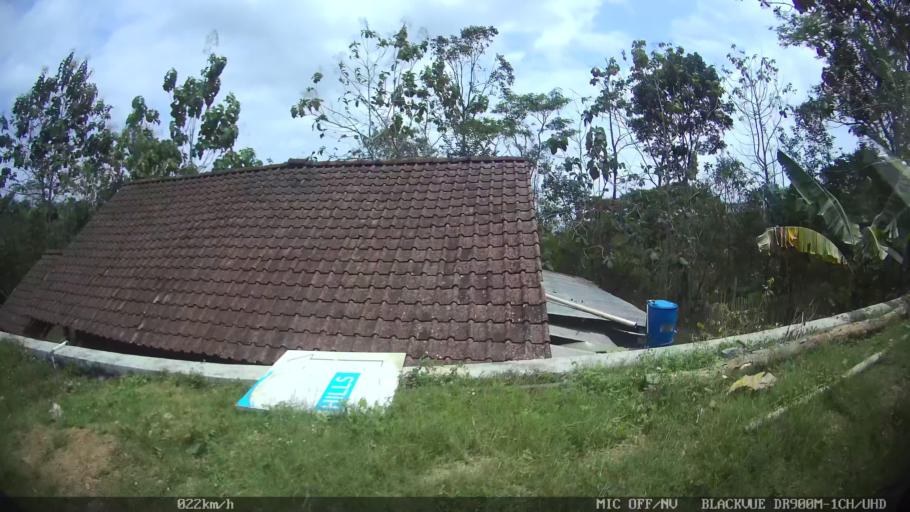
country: ID
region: Central Java
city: Candi Prambanan
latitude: -7.7929
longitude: 110.5183
